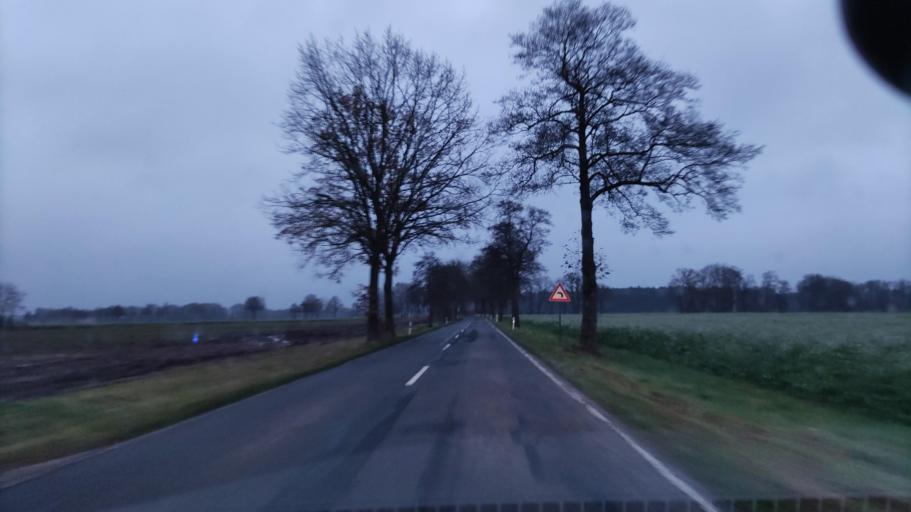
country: DE
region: Lower Saxony
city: Karwitz
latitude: 53.0269
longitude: 11.0197
